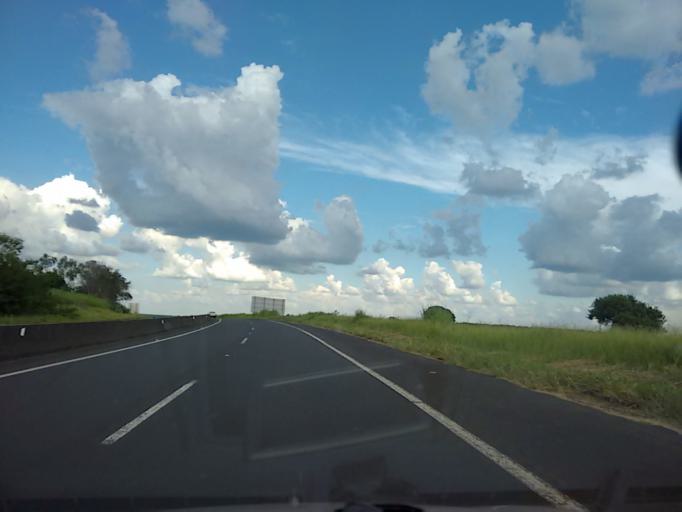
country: BR
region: Sao Paulo
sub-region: Marilia
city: Marilia
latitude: -22.2334
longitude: -49.8163
